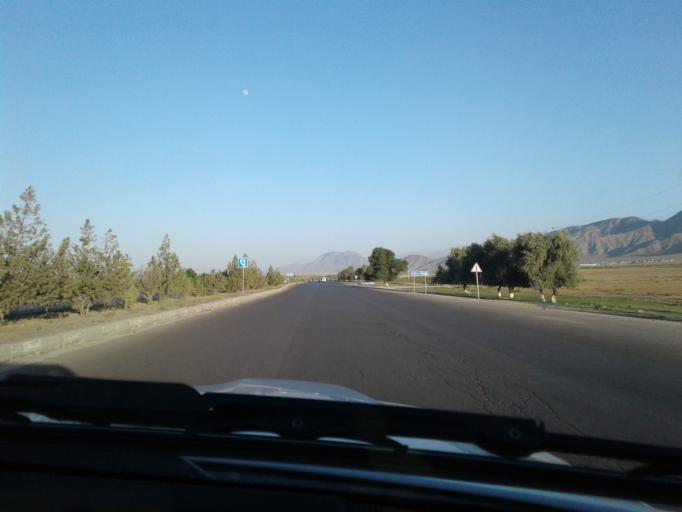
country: TM
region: Ahal
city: Arcabil
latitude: 38.2182
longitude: 57.8036
